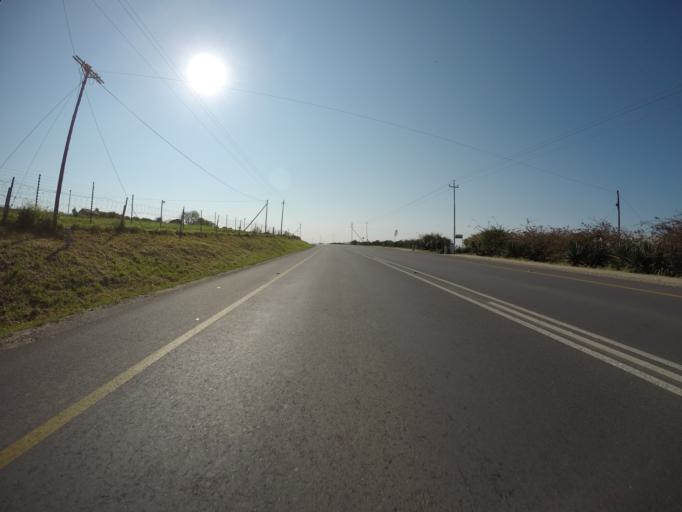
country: ZA
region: Western Cape
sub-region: Cape Winelands District Municipality
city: Noorder-Paarl
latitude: -33.6833
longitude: 18.9466
